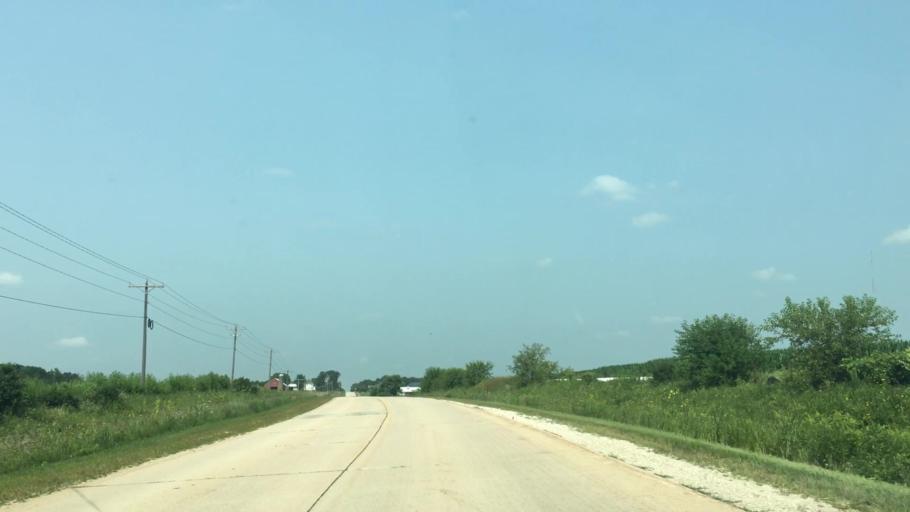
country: US
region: Iowa
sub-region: Fayette County
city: Oelwein
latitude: 42.6669
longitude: -91.8938
